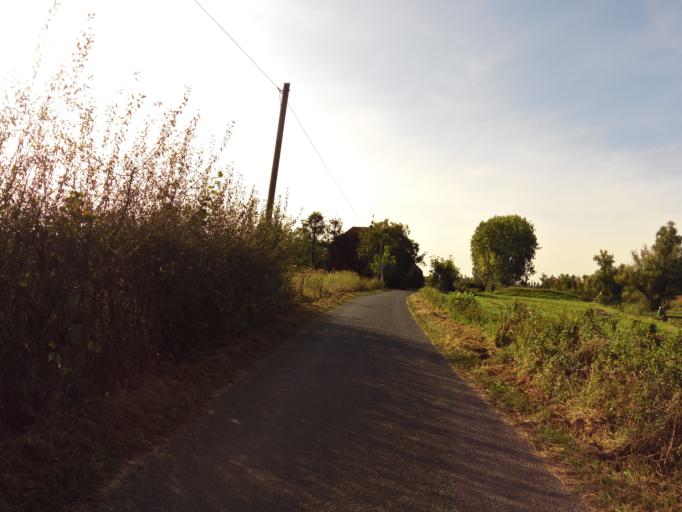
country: NL
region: Gelderland
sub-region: Gemeente Groesbeek
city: Berg en Dal
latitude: 51.8359
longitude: 5.9643
